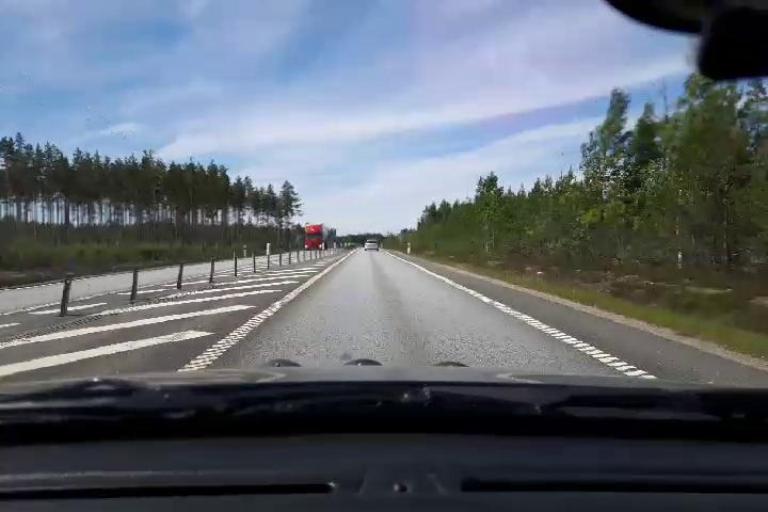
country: SE
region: Gaevleborg
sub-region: Gavle Kommun
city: Norrsundet
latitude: 61.0357
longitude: 16.9697
